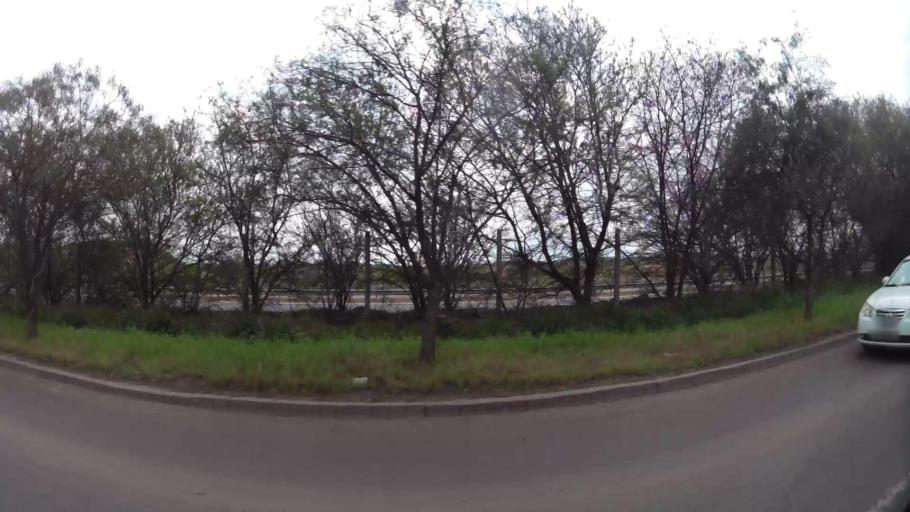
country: CL
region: Santiago Metropolitan
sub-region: Provincia de Chacabuco
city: Chicureo Abajo
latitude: -33.2010
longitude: -70.6616
